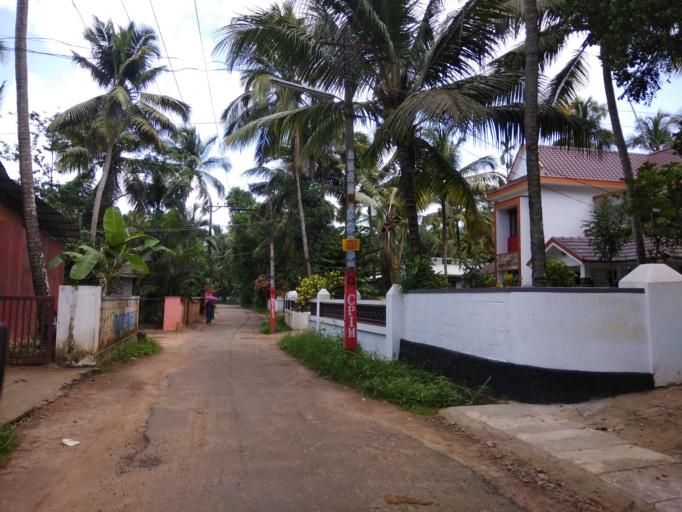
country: IN
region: Kerala
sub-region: Thrissur District
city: Avanoor
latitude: 10.5404
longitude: 76.1429
